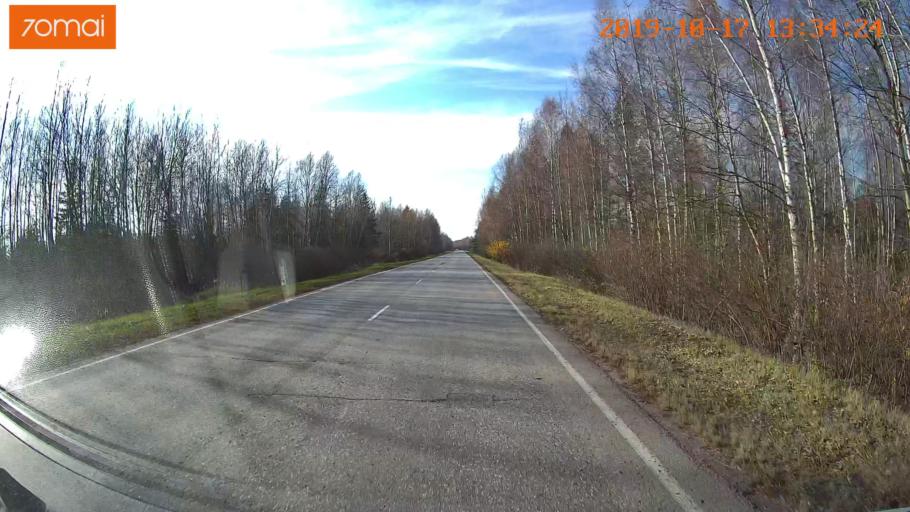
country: RU
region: Vladimir
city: Velikodvorskiy
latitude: 55.1443
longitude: 40.7168
